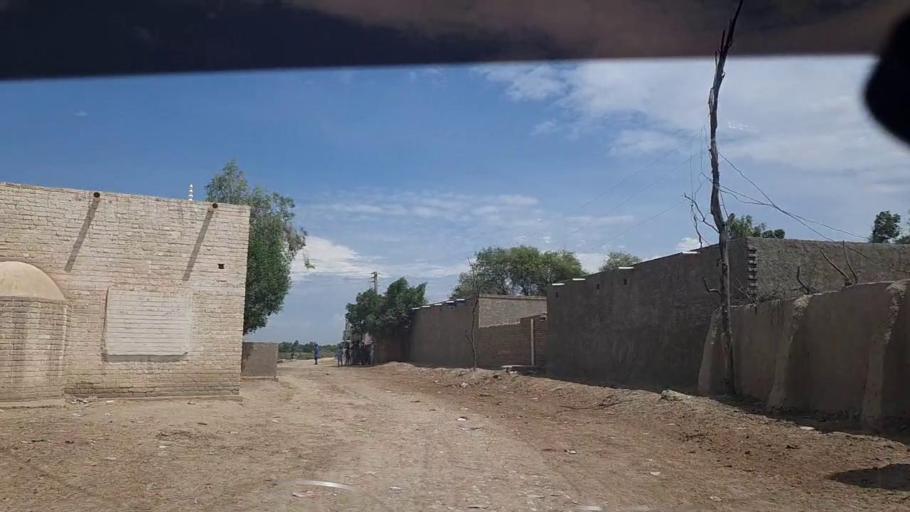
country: PK
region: Sindh
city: Ghauspur
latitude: 28.1510
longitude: 68.9468
